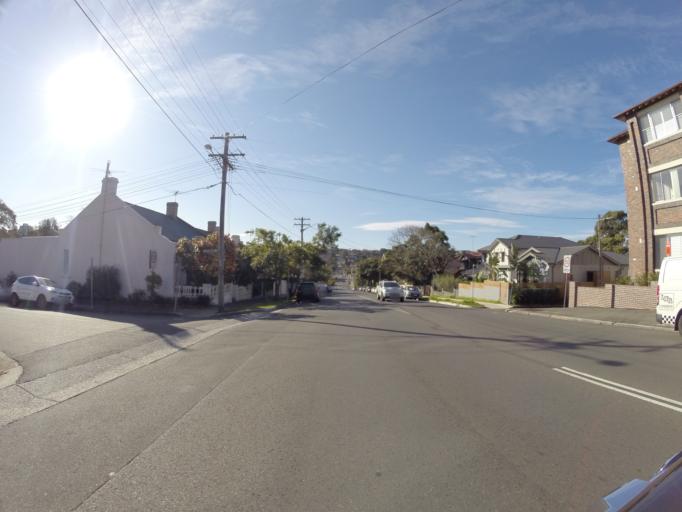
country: AU
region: New South Wales
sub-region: Randwick
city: Randwick
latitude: -33.9191
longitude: 151.2484
